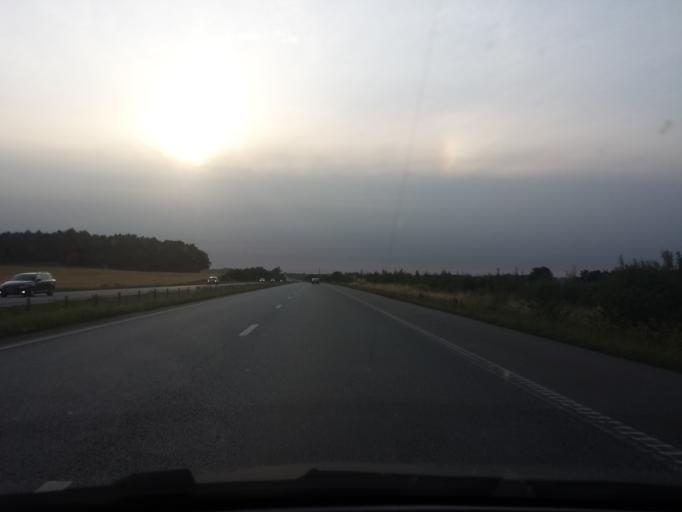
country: SE
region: Skane
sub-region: Malmo
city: Oxie
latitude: 55.5477
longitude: 13.1373
